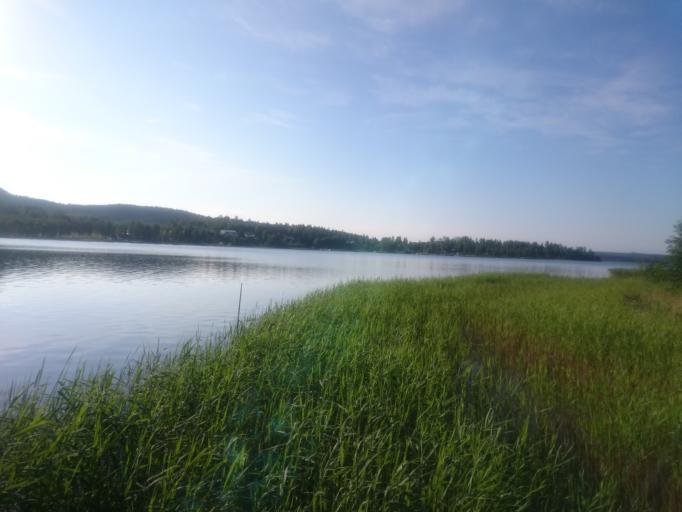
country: SE
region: Vaesternorrland
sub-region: OErnskoeldsviks Kommun
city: Ornskoldsvik
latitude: 63.2617
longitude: 18.8665
